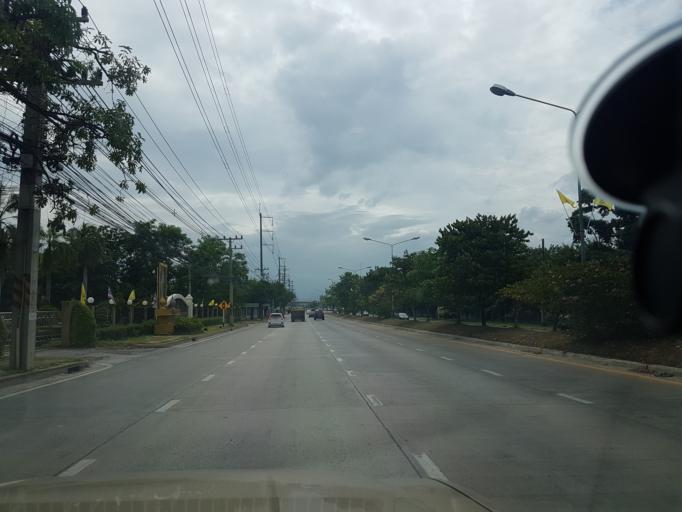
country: TH
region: Sara Buri
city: Phra Phutthabat
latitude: 14.7214
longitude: 100.8052
